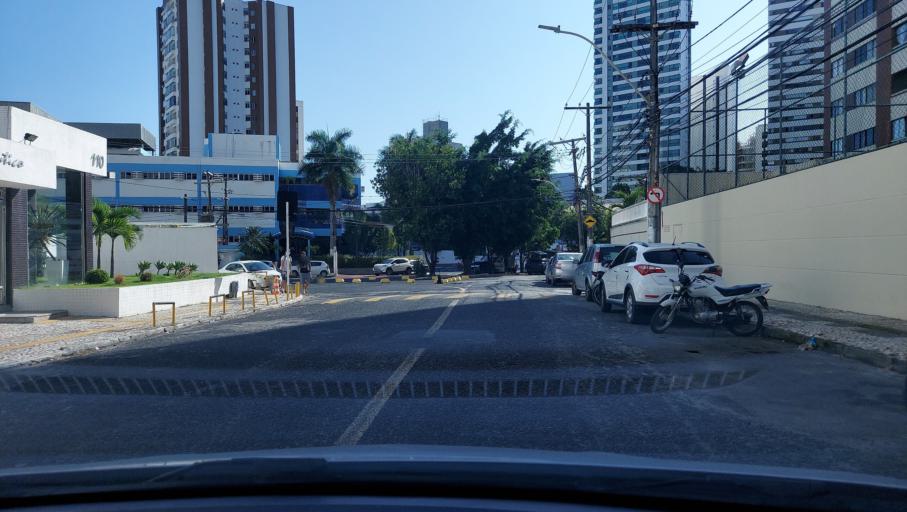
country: BR
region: Bahia
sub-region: Salvador
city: Salvador
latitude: -12.9887
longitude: -38.4522
